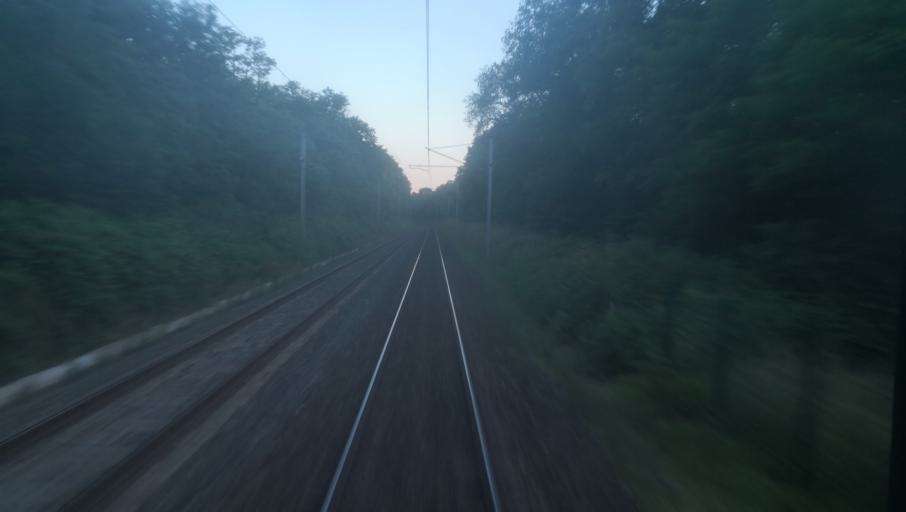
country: FR
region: Centre
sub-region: Departement du Cher
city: Saint-Satur
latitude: 47.3474
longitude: 2.8824
